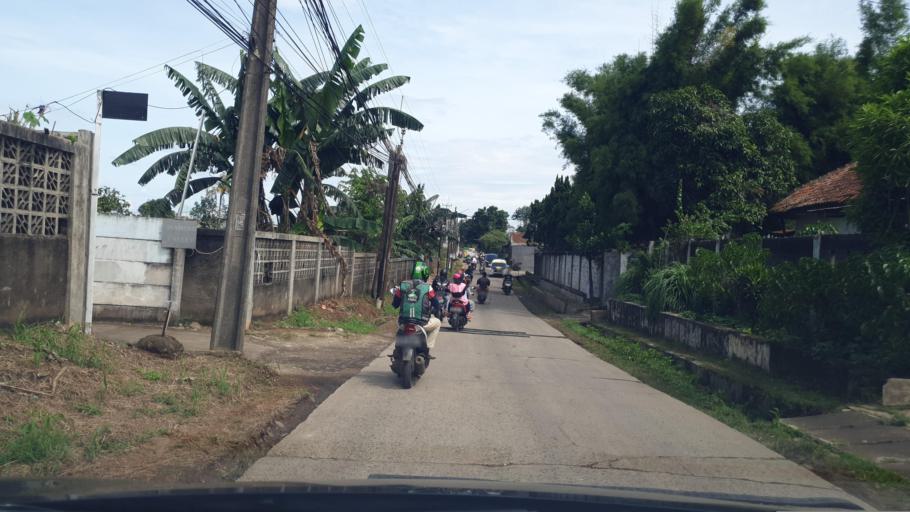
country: ID
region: West Java
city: Sawangan
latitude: -6.4079
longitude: 106.7702
